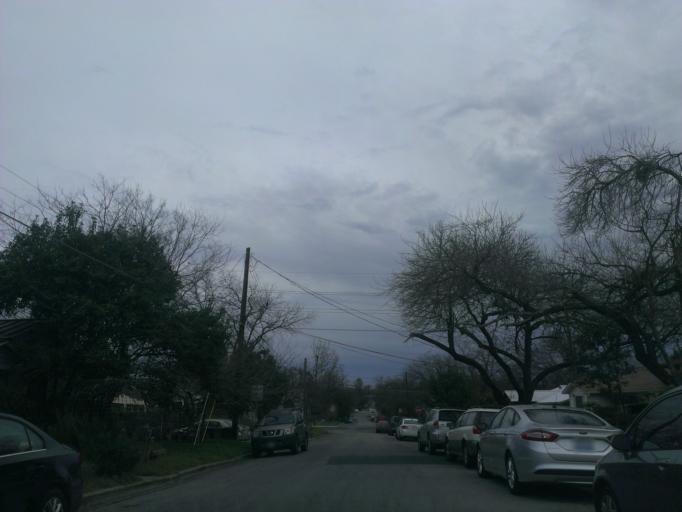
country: US
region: Texas
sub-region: Travis County
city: Austin
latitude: 30.2833
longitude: -97.7187
